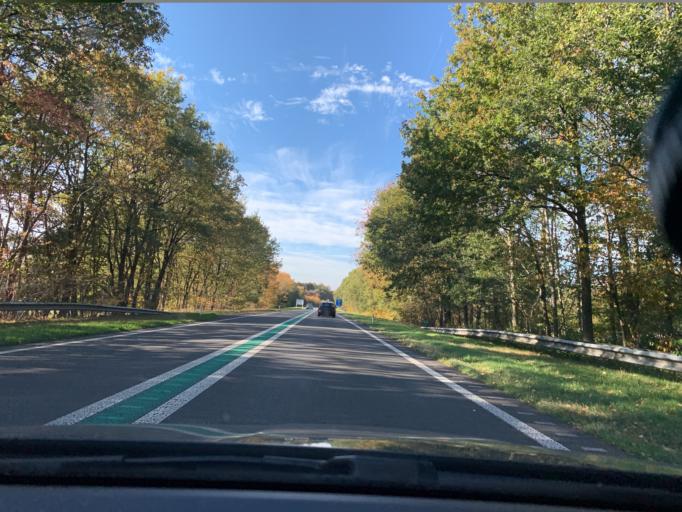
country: NL
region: Drenthe
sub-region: Gemeente Tynaarlo
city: Zuidlaren
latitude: 53.0802
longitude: 6.6695
